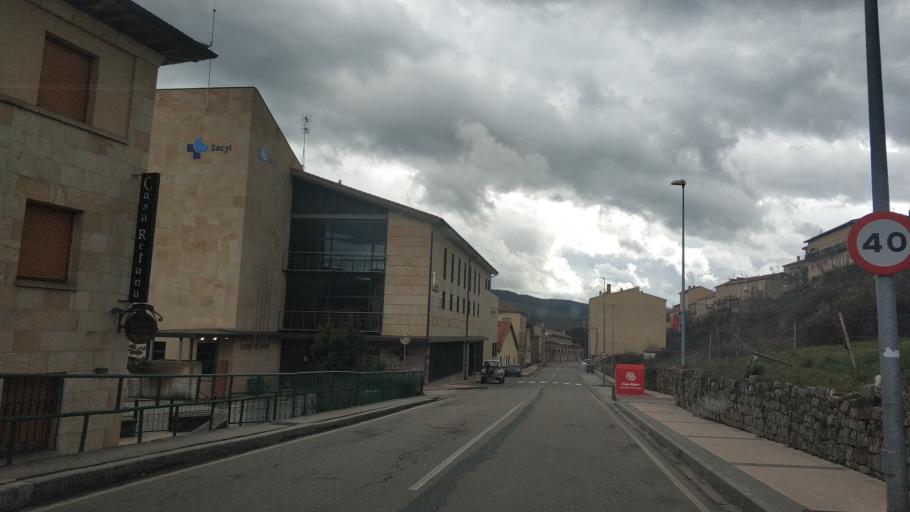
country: ES
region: Castille and Leon
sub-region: Provincia de Burgos
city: Quintanar de la Sierra
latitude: 41.9796
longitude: -3.0417
